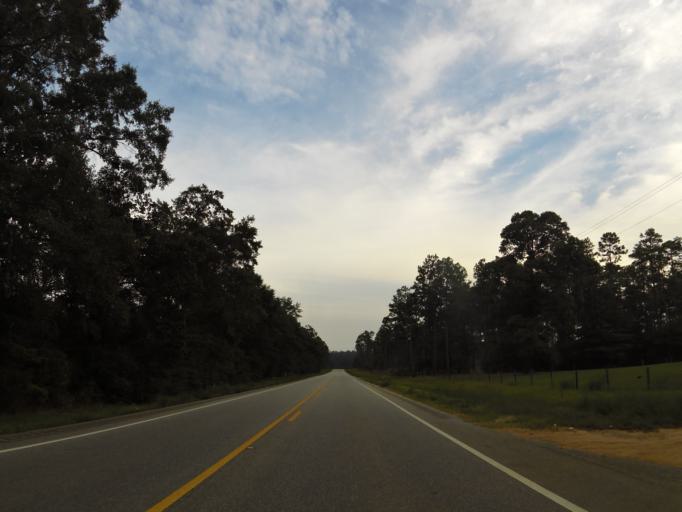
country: US
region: Alabama
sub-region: Monroe County
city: Frisco City
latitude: 31.2682
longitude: -87.4994
